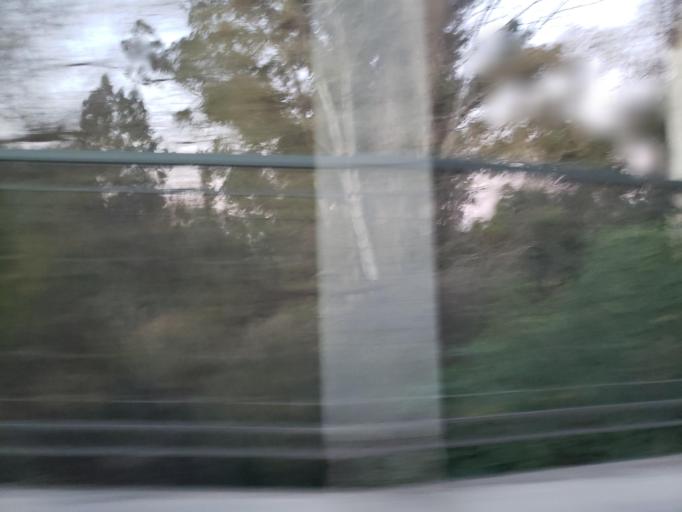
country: CL
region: Santiago Metropolitan
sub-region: Provincia de Talagante
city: El Monte
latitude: -33.6857
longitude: -70.9748
